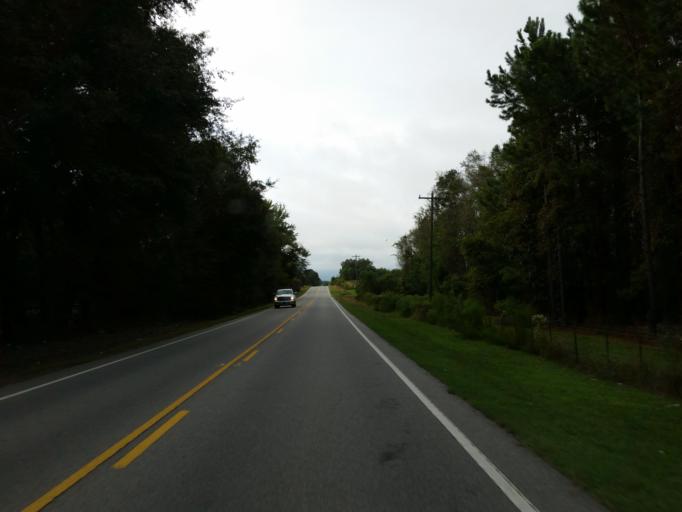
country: US
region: Georgia
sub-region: Tift County
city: Tifton
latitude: 31.5756
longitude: -83.5689
